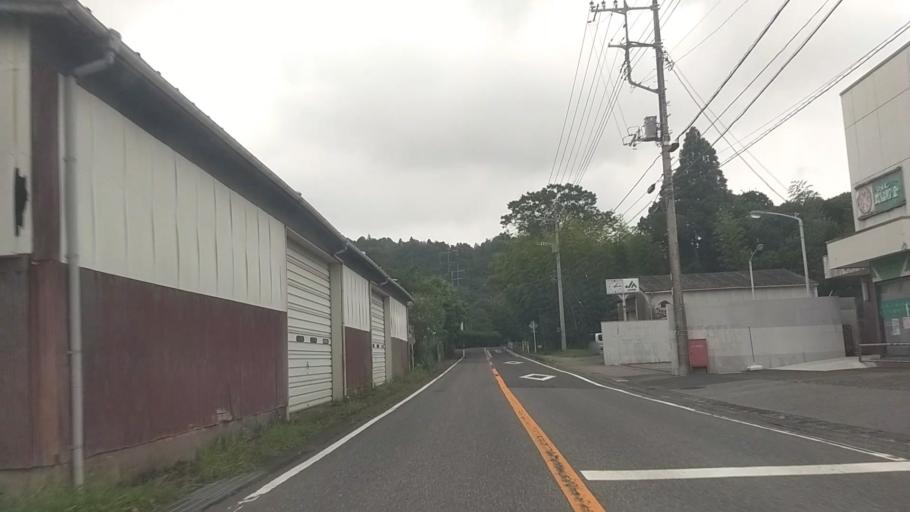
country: JP
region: Chiba
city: Katsuura
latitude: 35.2524
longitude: 140.2200
